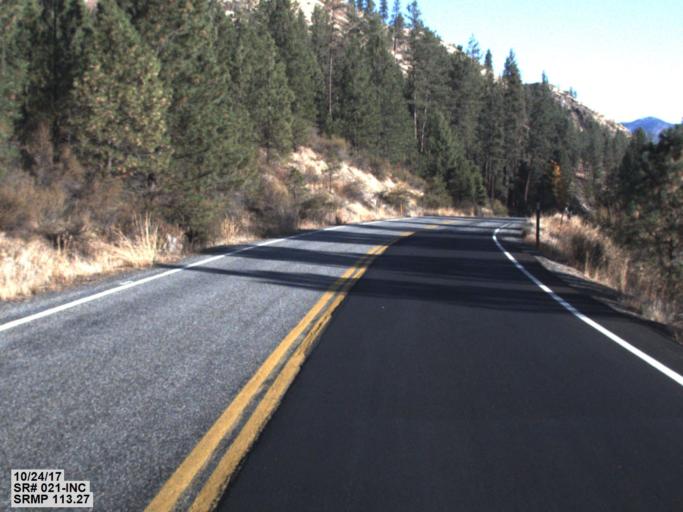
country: US
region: Washington
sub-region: Okanogan County
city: Coulee Dam
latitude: 48.0328
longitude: -118.6745
